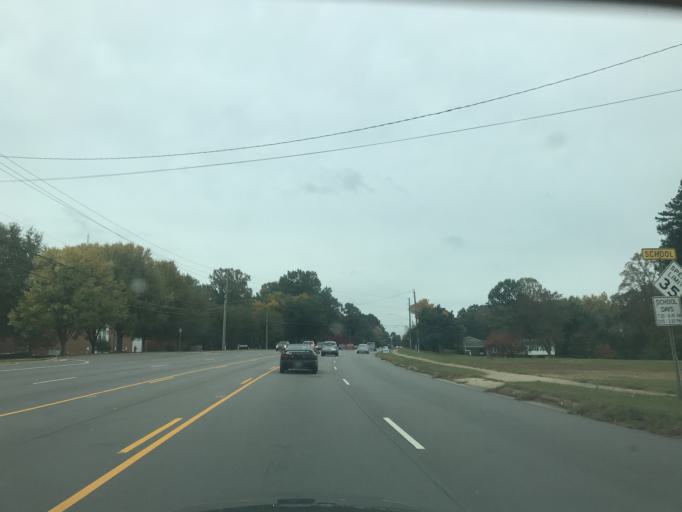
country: US
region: North Carolina
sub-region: Wake County
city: West Raleigh
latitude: 35.8579
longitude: -78.6165
